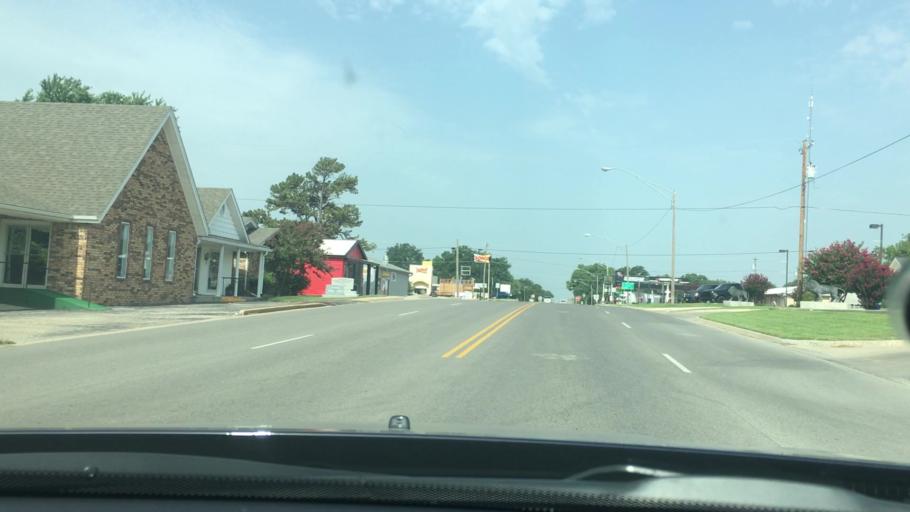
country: US
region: Oklahoma
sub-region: Garvin County
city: Stratford
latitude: 34.7967
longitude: -96.9647
